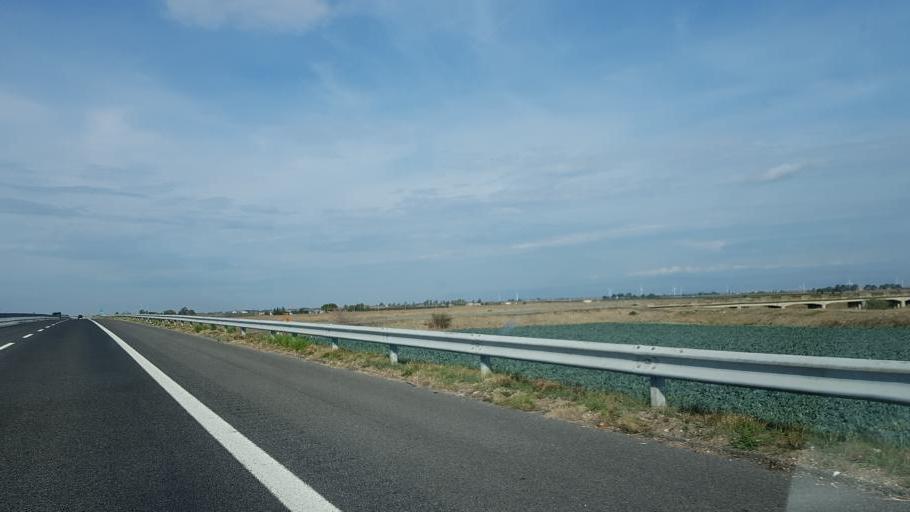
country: IT
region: Apulia
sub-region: Provincia di Foggia
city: Carapelle
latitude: 41.3779
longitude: 15.7580
